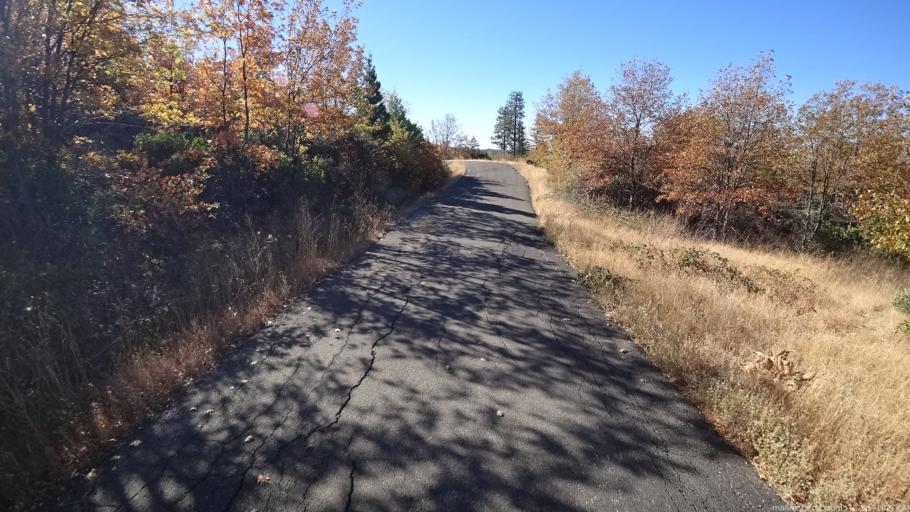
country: US
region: California
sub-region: Shasta County
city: Burney
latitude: 40.8011
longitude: -121.8967
